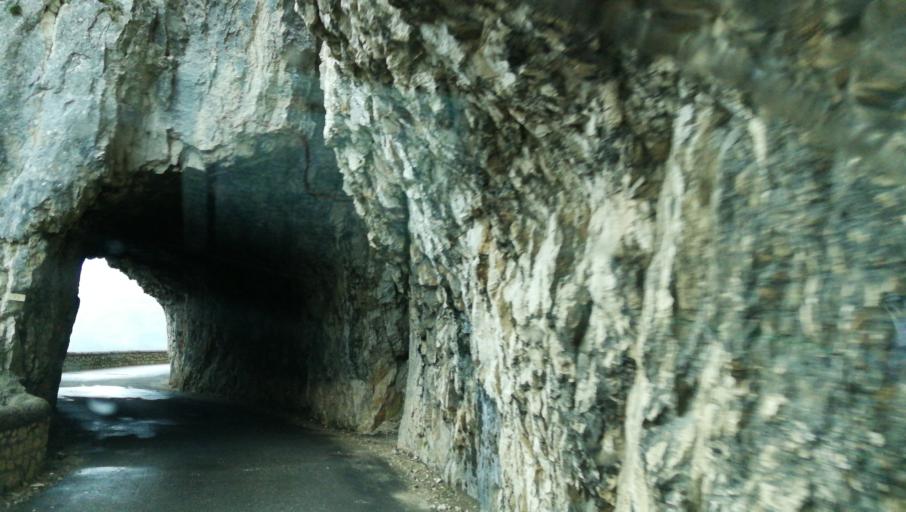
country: FR
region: Rhone-Alpes
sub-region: Departement de la Drome
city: Saint-Laurent-en-Royans
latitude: 44.9998
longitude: 5.3334
